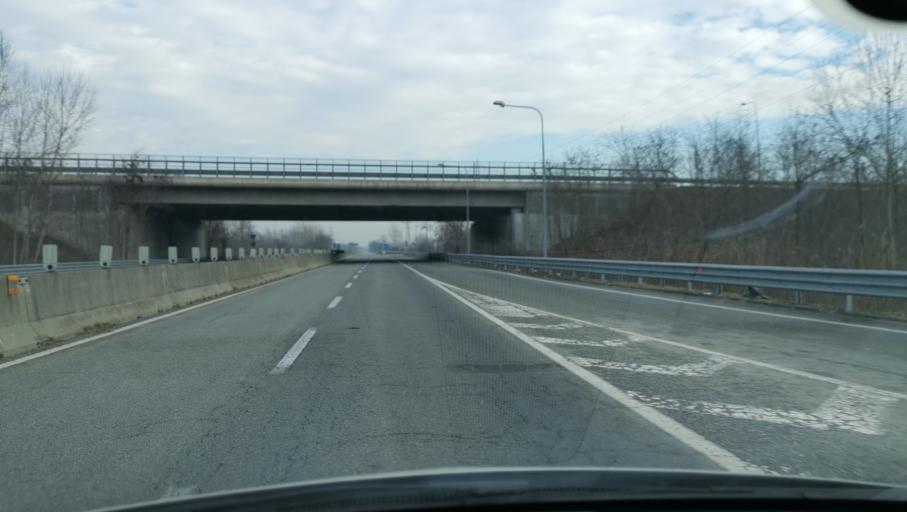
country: IT
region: Piedmont
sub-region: Provincia di Torino
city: Brandizzo
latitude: 45.1610
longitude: 7.8219
